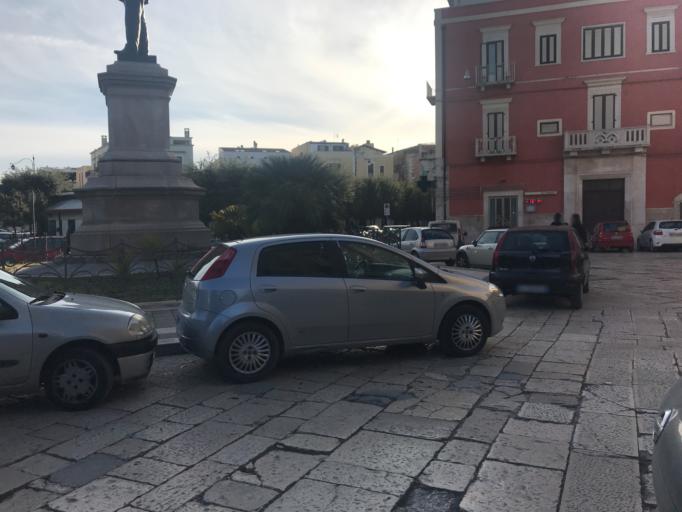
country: IT
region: Apulia
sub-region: Provincia di Bari
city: Corato
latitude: 41.1518
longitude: 16.4127
